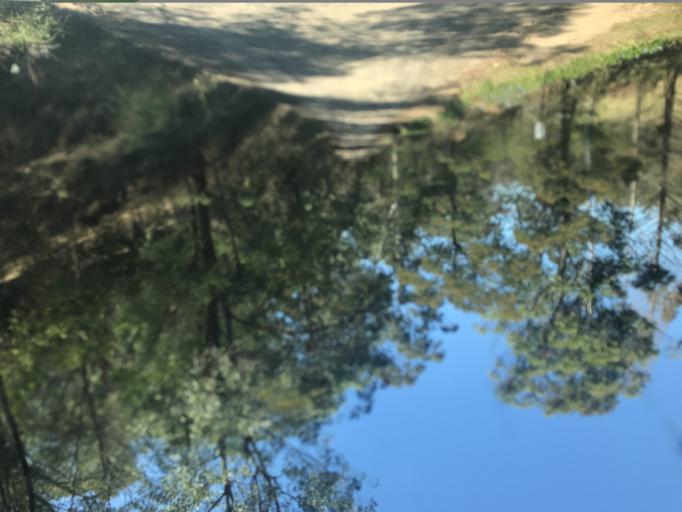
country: AU
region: New South Wales
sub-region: Wyong Shire
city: Little Jilliby
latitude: -33.1961
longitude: 151.0110
